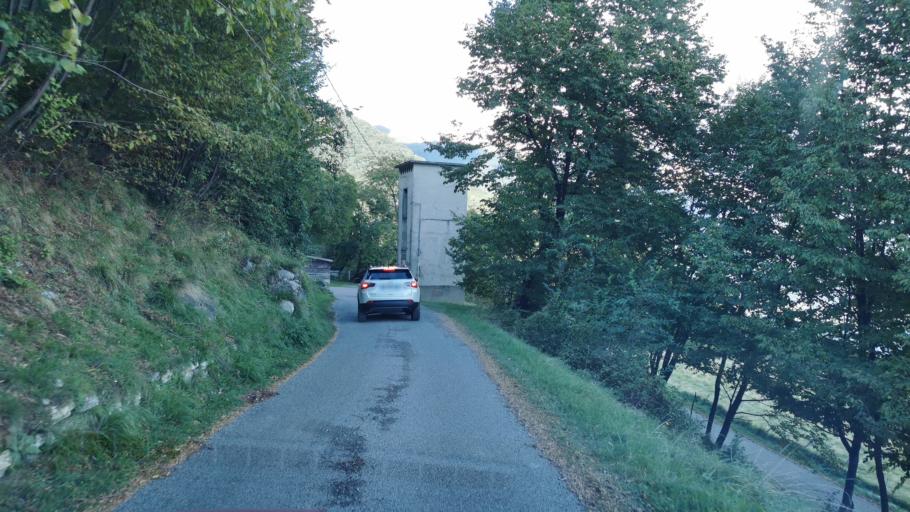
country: IT
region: Lombardy
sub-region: Provincia di Como
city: Moltrasio
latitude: 45.8613
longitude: 9.0865
